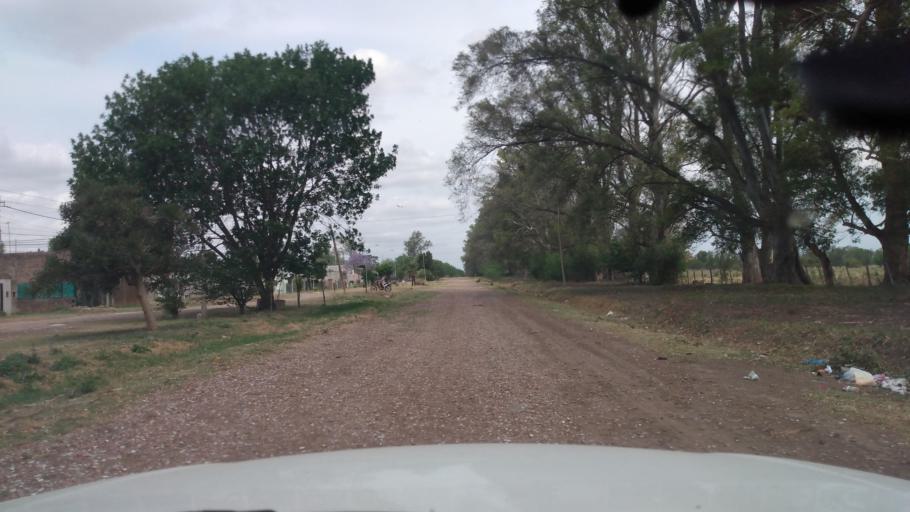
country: AR
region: Buenos Aires
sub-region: Partido de Lujan
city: Lujan
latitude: -34.5585
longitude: -59.2079
